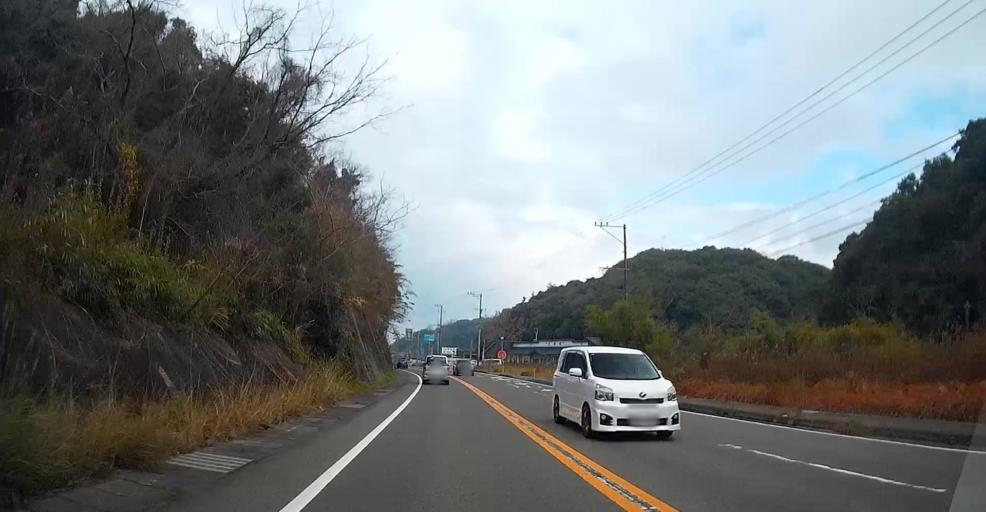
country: JP
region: Kumamoto
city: Yatsushiro
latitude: 32.5615
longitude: 130.4136
